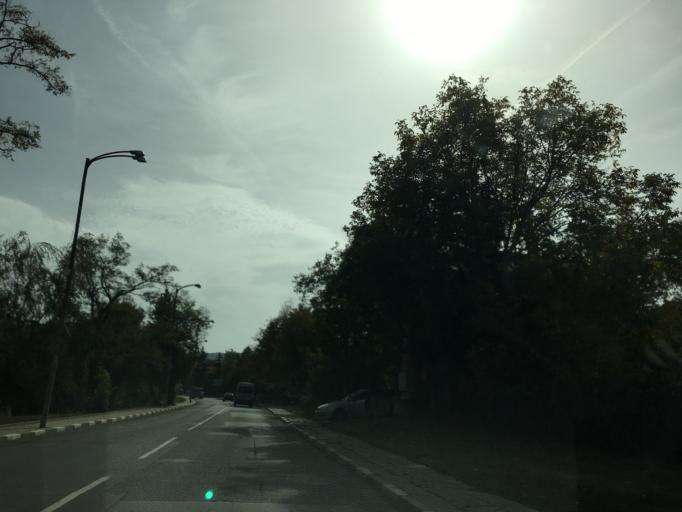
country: BG
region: Sofia-Capital
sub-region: Stolichna Obshtina
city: Sofia
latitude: 42.5867
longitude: 23.4206
